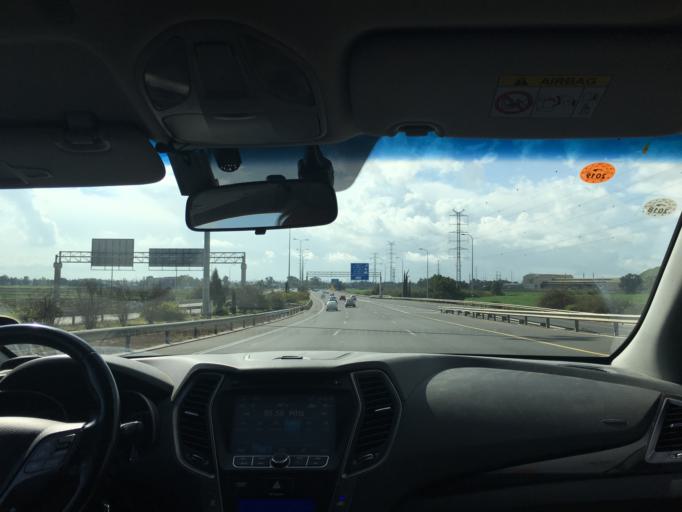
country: IL
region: Tel Aviv
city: Azor
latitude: 32.0359
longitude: 34.8294
